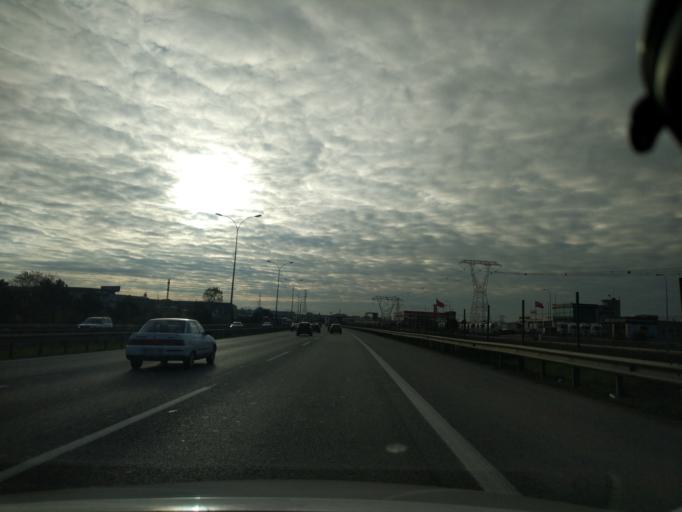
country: TR
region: Istanbul
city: Icmeler
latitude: 40.9112
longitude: 29.3568
